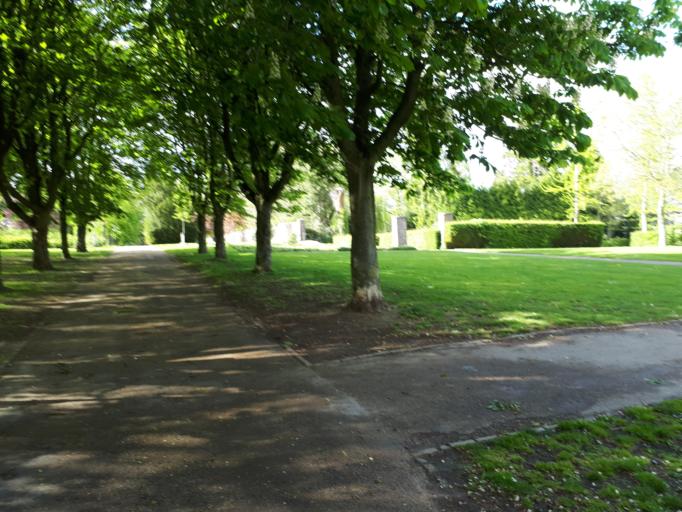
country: NL
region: Limburg
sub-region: Gemeente Vaals
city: Vaals
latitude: 50.7712
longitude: 6.0132
